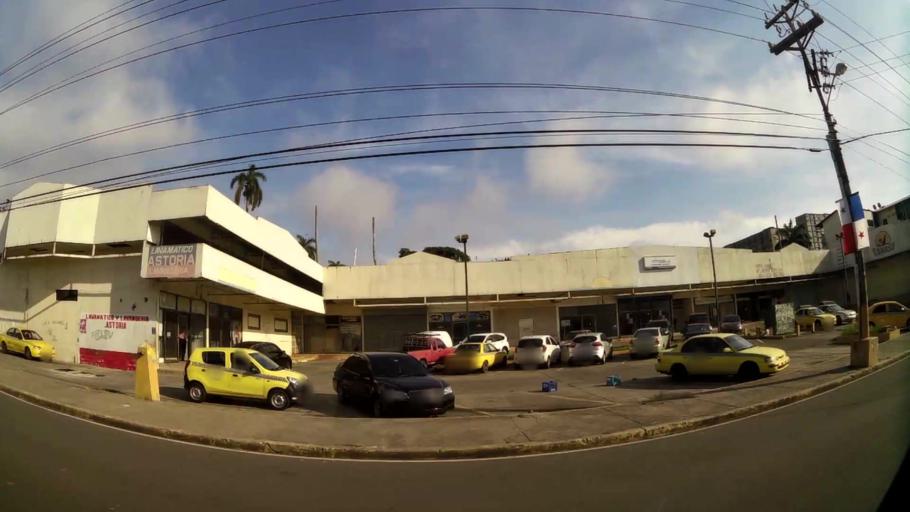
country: PA
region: Panama
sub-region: Distrito de Panama
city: Ancon
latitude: 8.9510
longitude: -79.5451
